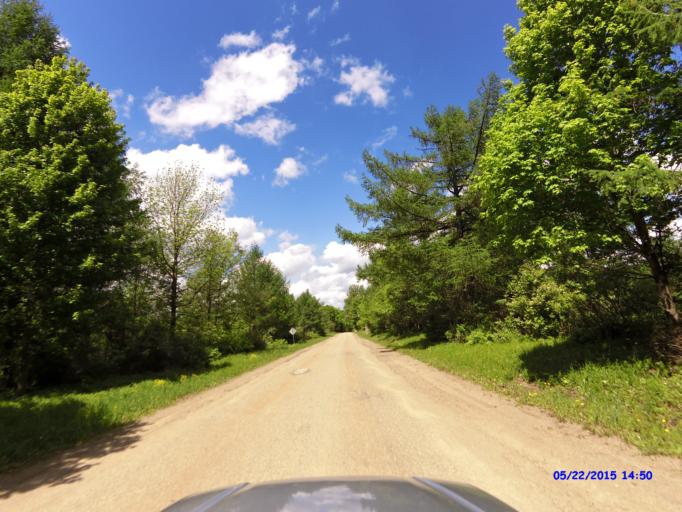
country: US
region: New York
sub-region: Cattaraugus County
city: Franklinville
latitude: 42.3634
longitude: -78.5840
